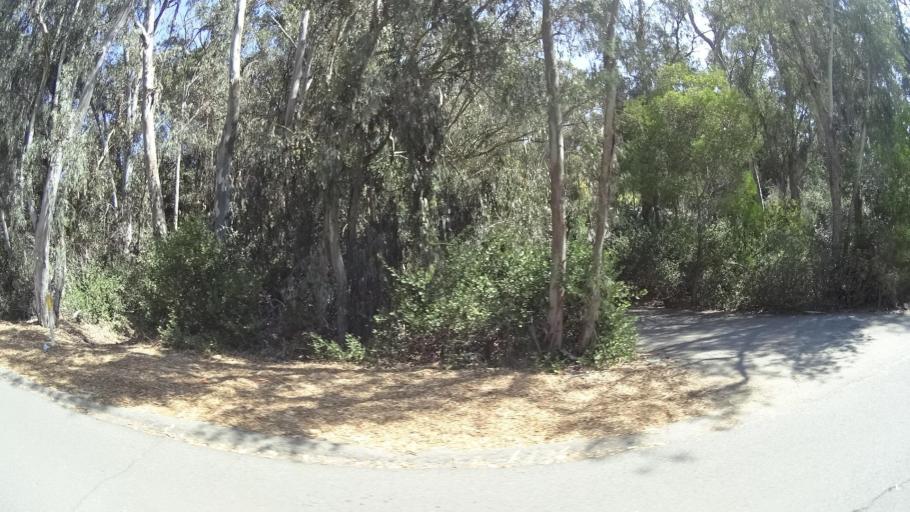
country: US
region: California
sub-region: San Diego County
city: Rancho Santa Fe
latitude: 33.0002
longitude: -117.2156
